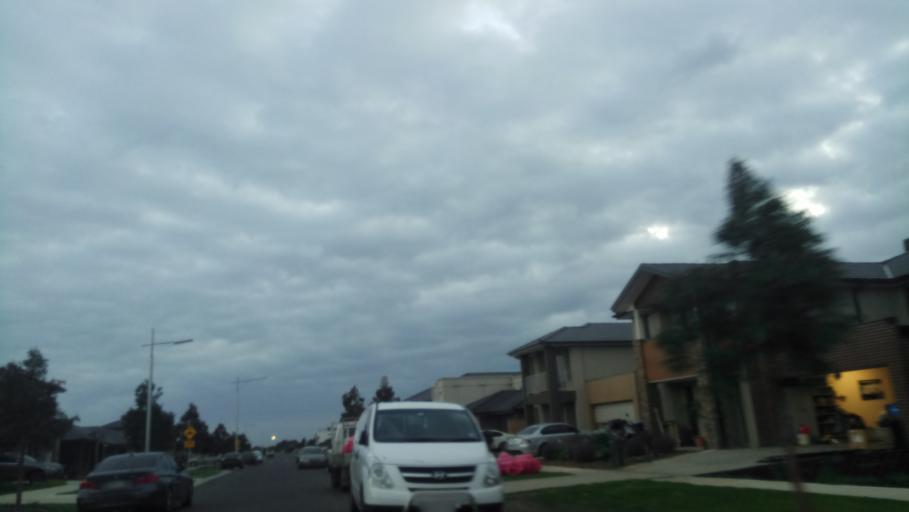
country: AU
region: Victoria
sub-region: Wyndham
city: Point Cook
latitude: -37.9127
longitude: 144.7604
